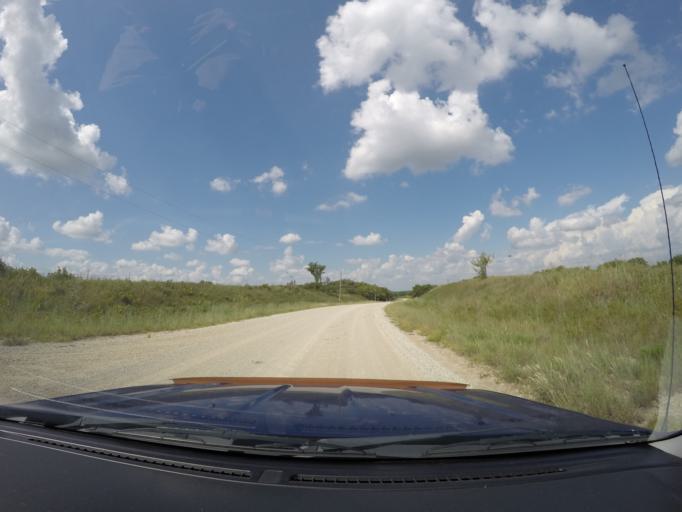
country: US
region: Kansas
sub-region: Riley County
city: Manhattan
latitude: 39.1176
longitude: -96.4606
